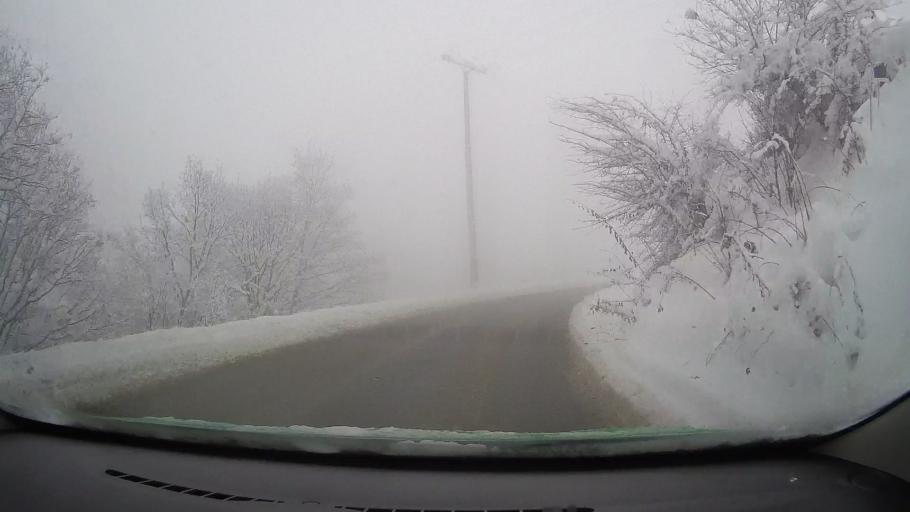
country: RO
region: Sibiu
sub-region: Comuna Poiana Sibiului
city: Poiana Sibiului
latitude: 45.8066
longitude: 23.7472
